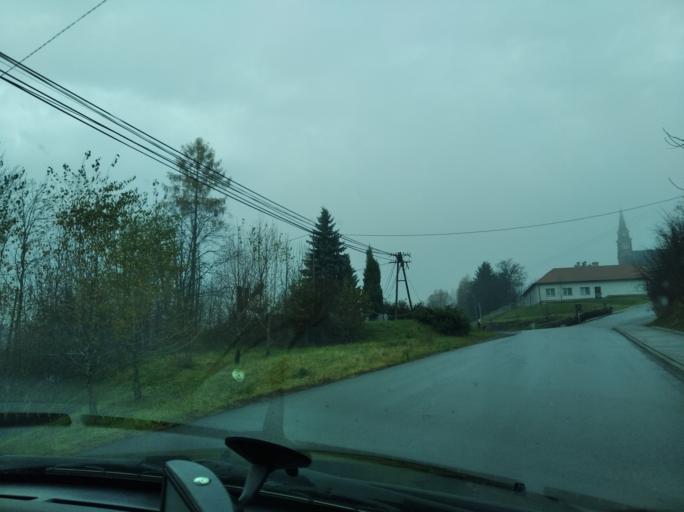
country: PL
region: Subcarpathian Voivodeship
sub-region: Powiat rzeszowski
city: Lubenia
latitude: 49.9297
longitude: 21.9268
